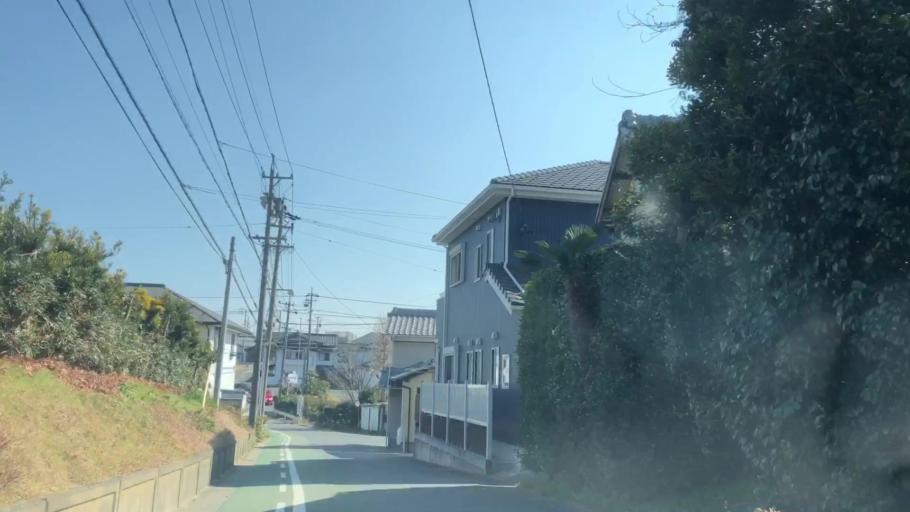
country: JP
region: Aichi
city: Tahara
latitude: 34.6653
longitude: 137.2575
